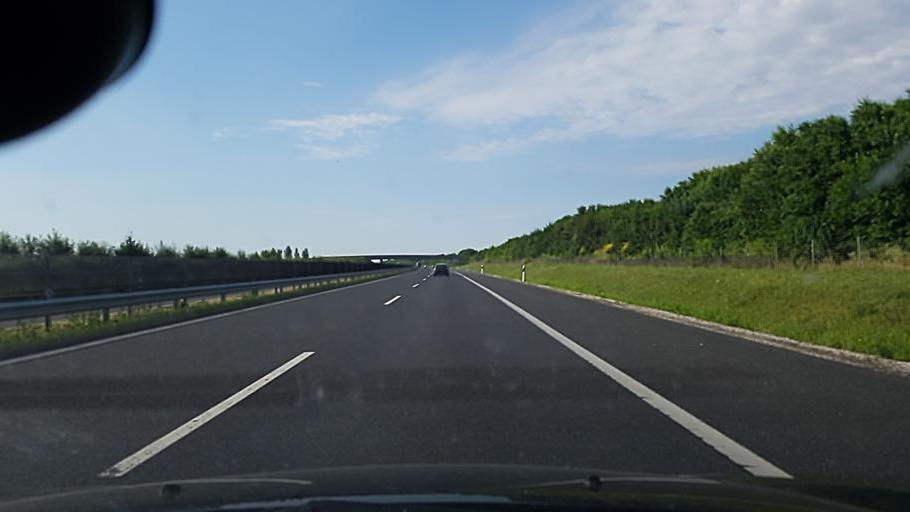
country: HU
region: Fejer
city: Ivancsa
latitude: 47.1532
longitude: 18.8043
